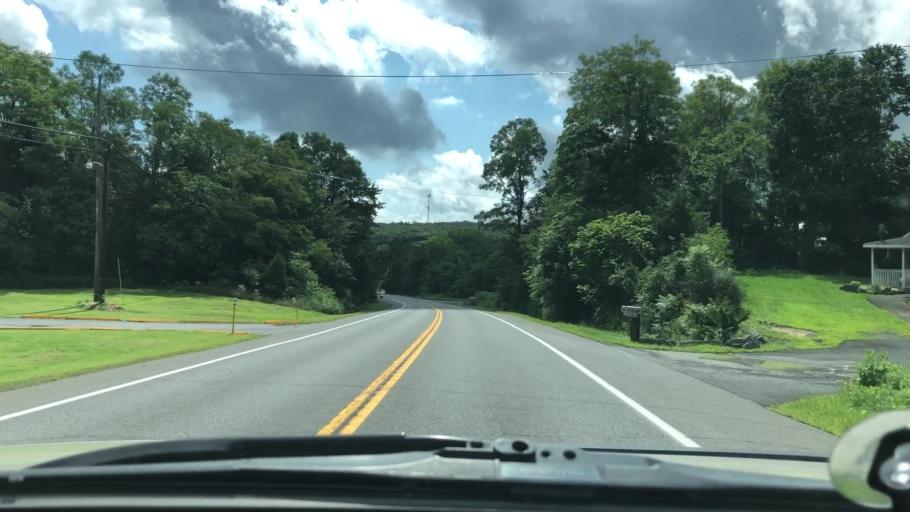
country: US
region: New York
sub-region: Ulster County
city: Manorville
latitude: 42.1216
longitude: -73.9928
